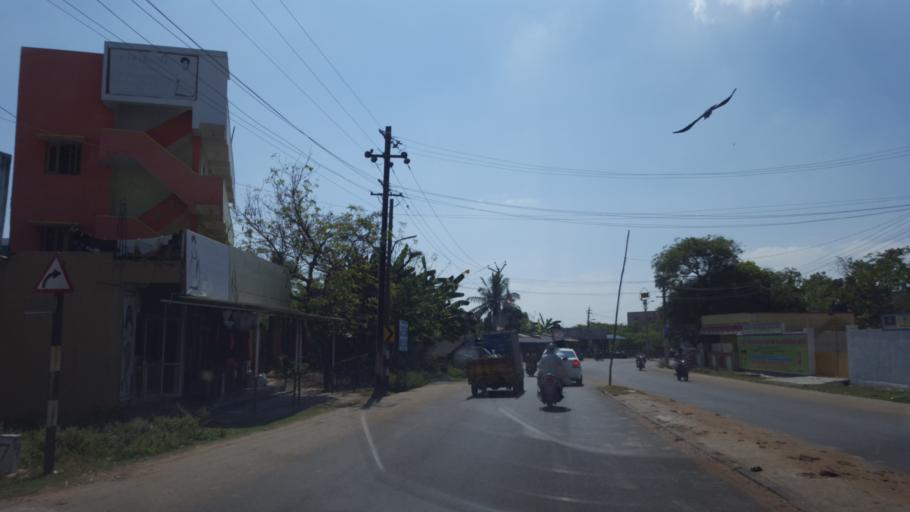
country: IN
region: Tamil Nadu
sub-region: Kancheepuram
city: Karumbakkam
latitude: 12.7190
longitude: 80.1883
